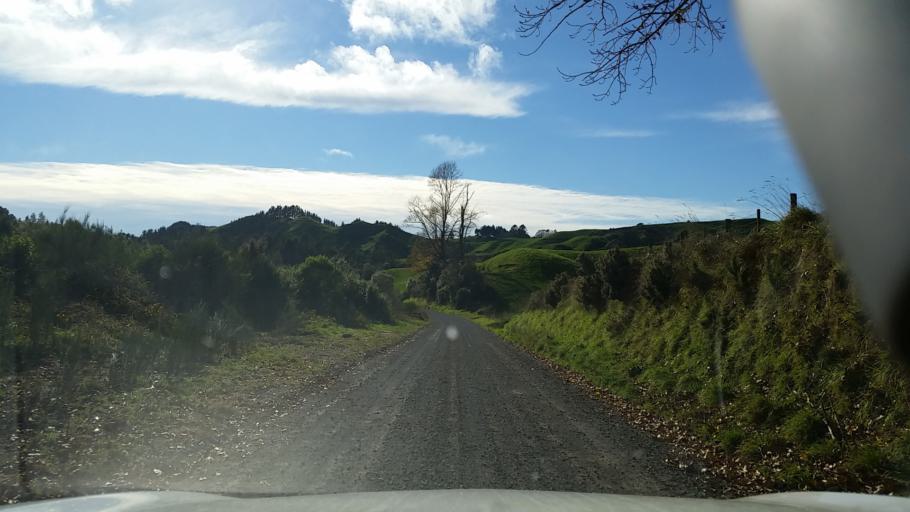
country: NZ
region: Bay of Plenty
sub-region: Rotorua District
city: Rotorua
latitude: -38.3617
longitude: 176.2097
